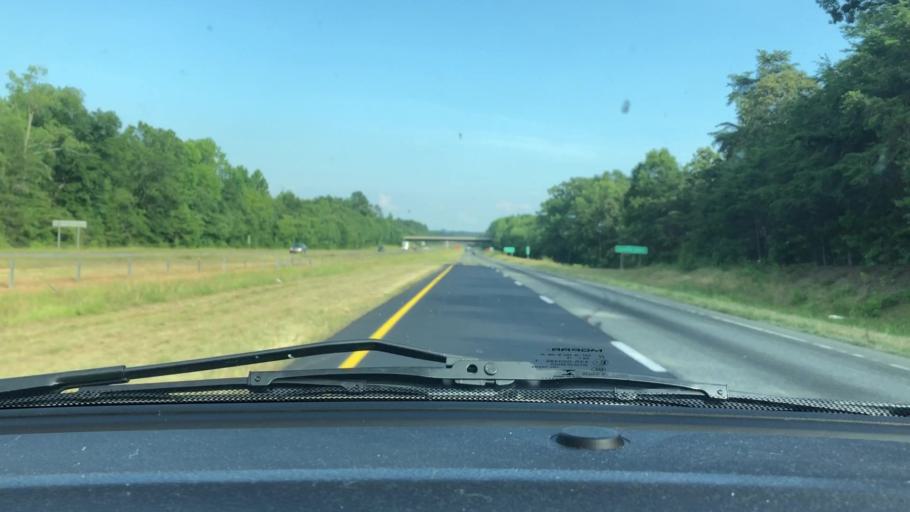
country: US
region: North Carolina
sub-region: Randolph County
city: Liberty
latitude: 35.8064
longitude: -79.5443
